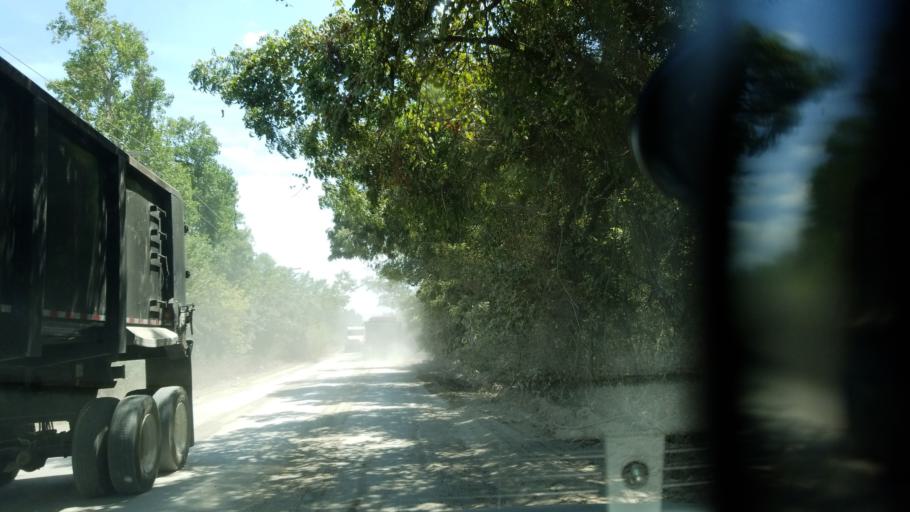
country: US
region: Texas
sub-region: Dallas County
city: Farmers Branch
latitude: 32.8775
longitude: -96.9198
